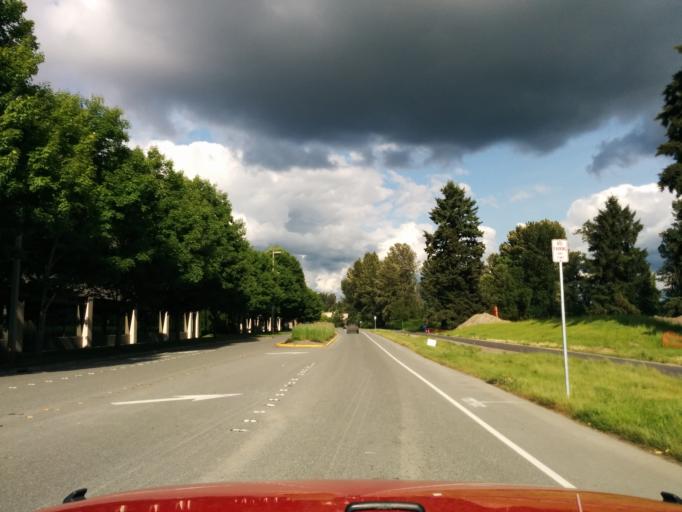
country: US
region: Washington
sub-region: King County
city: Redmond
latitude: 47.6684
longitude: -122.1188
